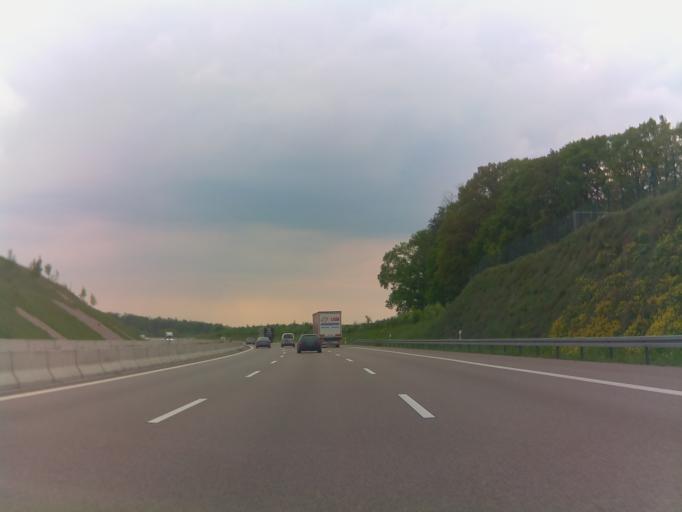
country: DE
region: Baden-Wuerttemberg
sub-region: Karlsruhe Region
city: Friolzheim
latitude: 48.8384
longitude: 8.8473
